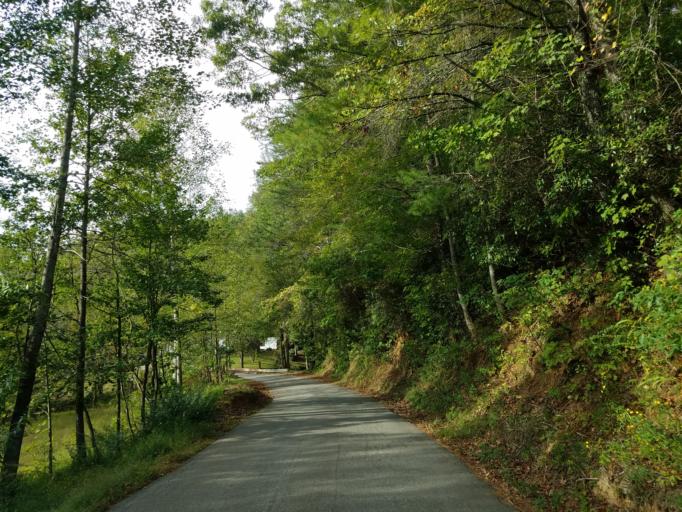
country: US
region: Georgia
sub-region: Dawson County
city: Dawsonville
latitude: 34.5697
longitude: -84.1526
